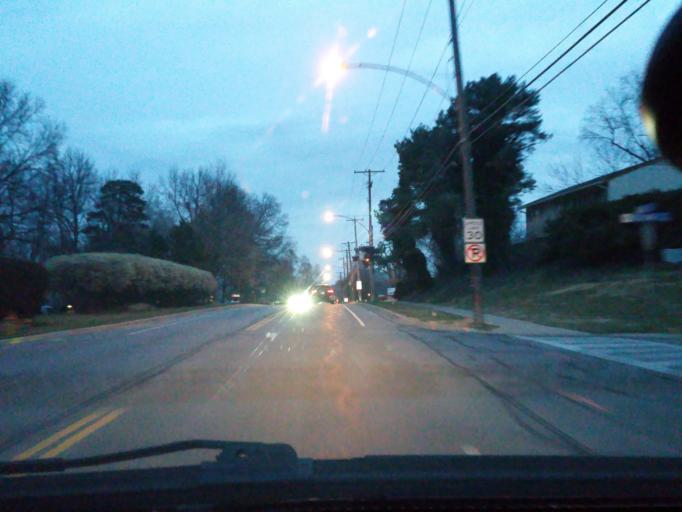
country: US
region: Kansas
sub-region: Johnson County
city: Fairway
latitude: 39.0124
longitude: -94.6304
